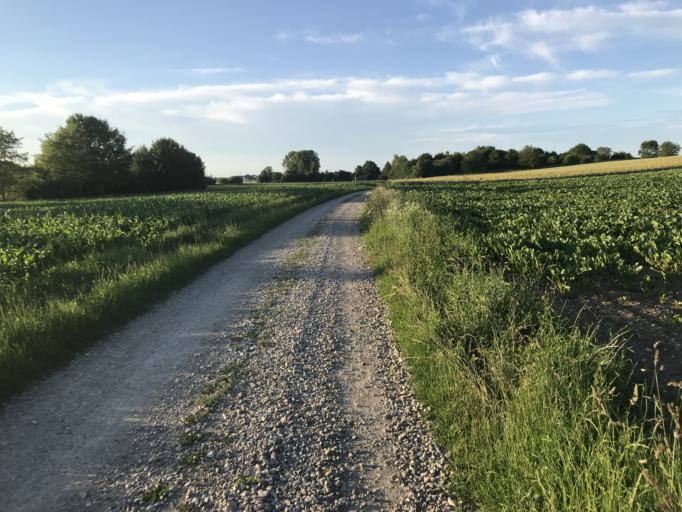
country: DE
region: Bavaria
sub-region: Swabia
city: Merching
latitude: 48.2547
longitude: 10.9669
